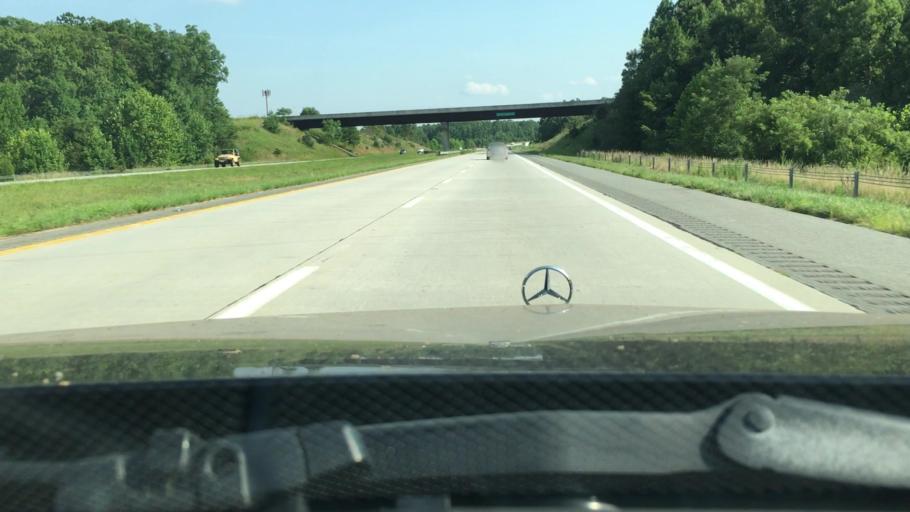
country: US
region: Virginia
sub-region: Amherst County
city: Amherst
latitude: 37.5245
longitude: -79.0644
